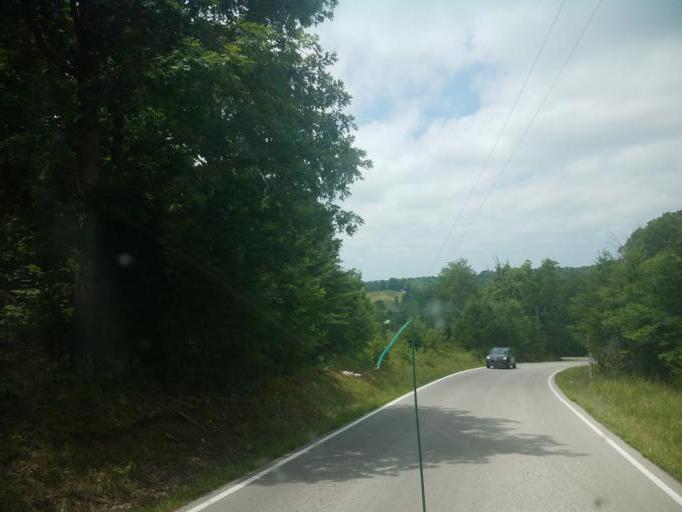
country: US
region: Kentucky
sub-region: Hart County
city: Munfordville
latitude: 37.3316
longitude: -86.0014
